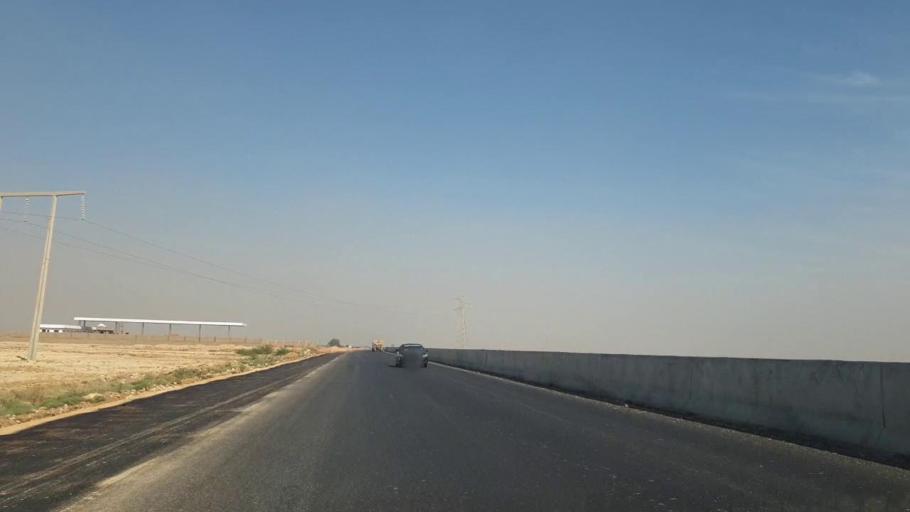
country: PK
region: Sindh
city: Jamshoro
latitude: 25.5337
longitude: 68.2832
